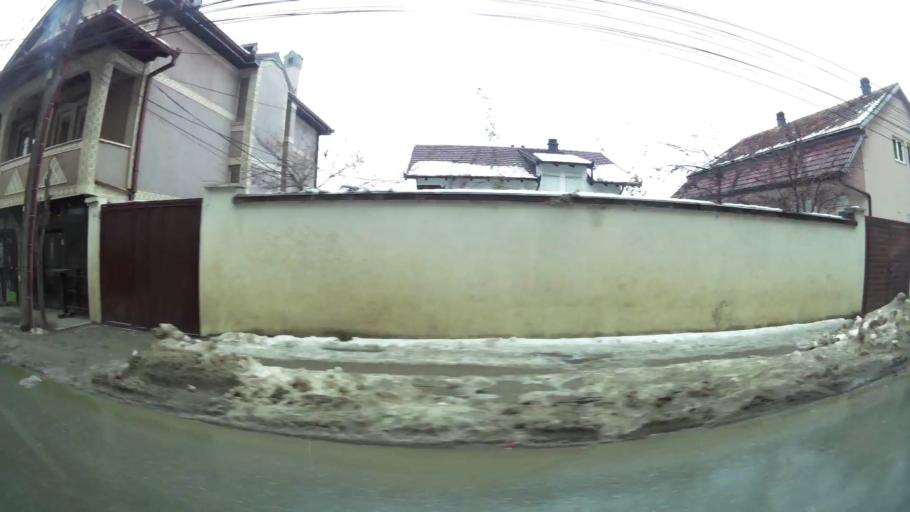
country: XK
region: Pristina
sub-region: Komuna e Prishtines
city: Pristina
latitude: 42.6810
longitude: 21.1778
